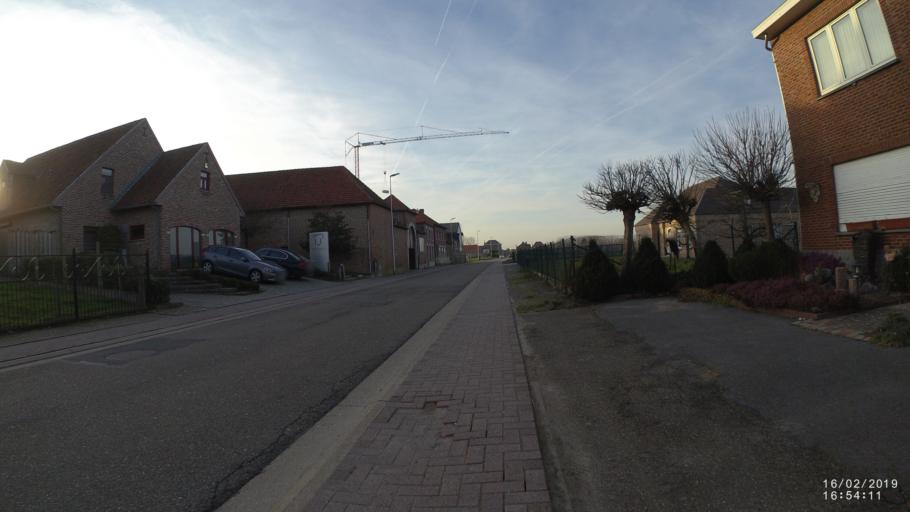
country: BE
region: Flanders
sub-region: Provincie Vlaams-Brabant
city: Zoutleeuw
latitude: 50.8213
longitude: 5.1382
